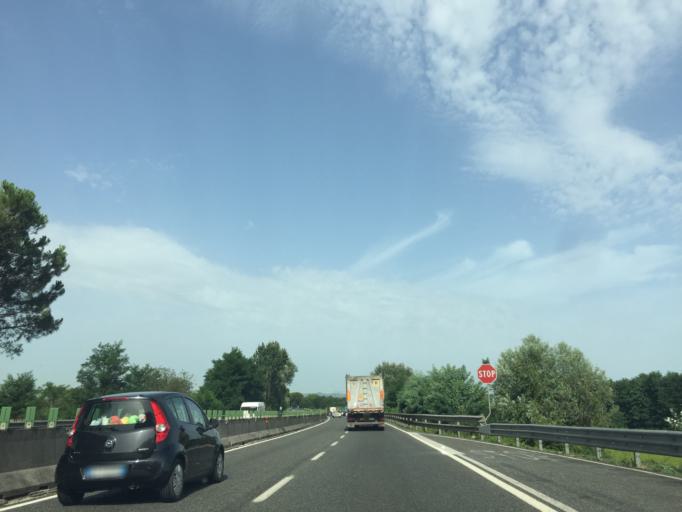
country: IT
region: Tuscany
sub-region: Province of Florence
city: San Pierino
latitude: 43.6985
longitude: 10.8187
